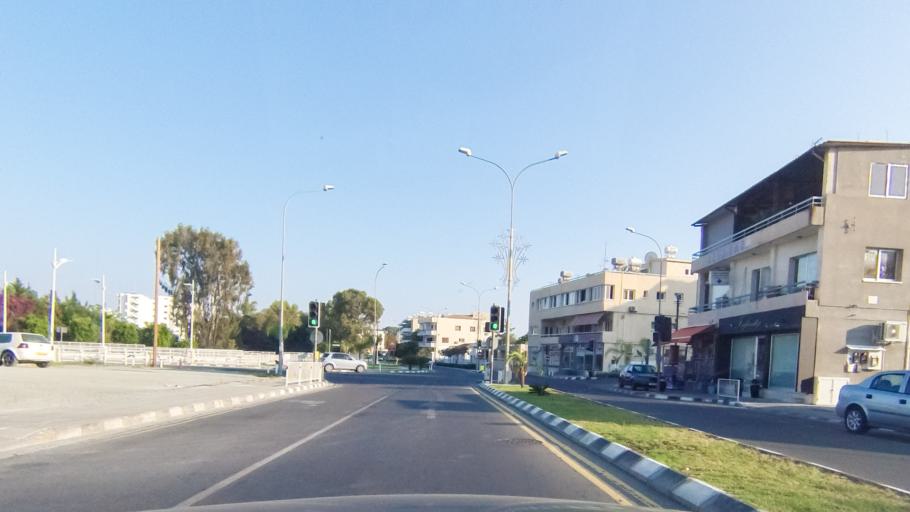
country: CY
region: Limassol
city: Mouttagiaka
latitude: 34.7000
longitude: 33.0880
